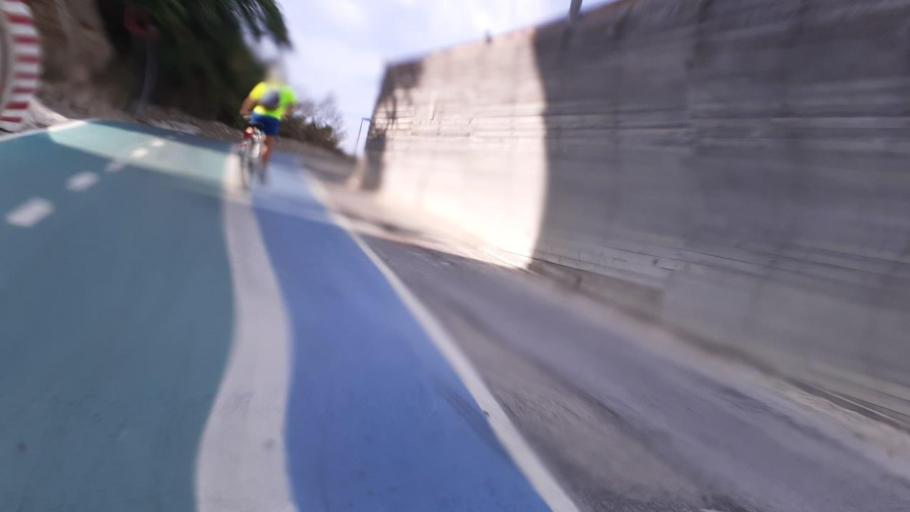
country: IT
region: Abruzzo
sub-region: Provincia di Chieti
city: Ortona
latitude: 42.3590
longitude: 14.4081
